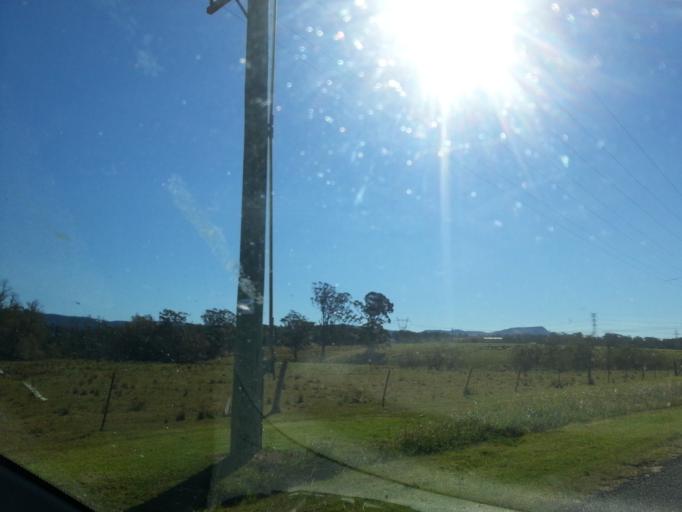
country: AU
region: New South Wales
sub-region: Wollongong
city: Dapto
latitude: -34.5277
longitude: 150.7757
